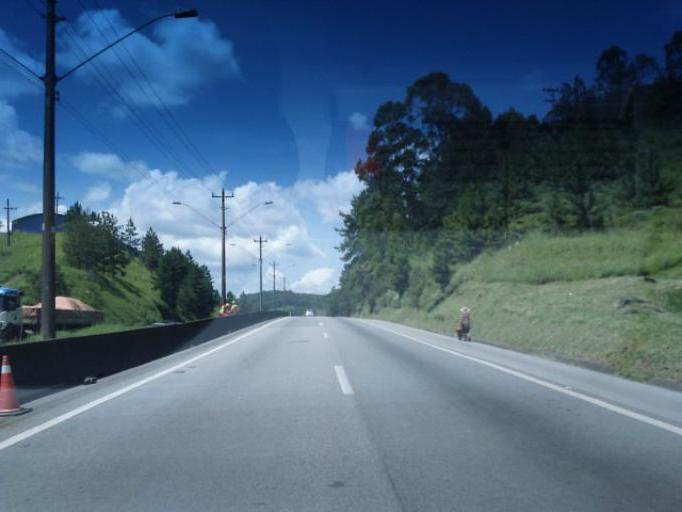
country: BR
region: Sao Paulo
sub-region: Sao Lourenco Da Serra
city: Sao Lourenco da Serra
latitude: -23.8993
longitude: -46.9884
